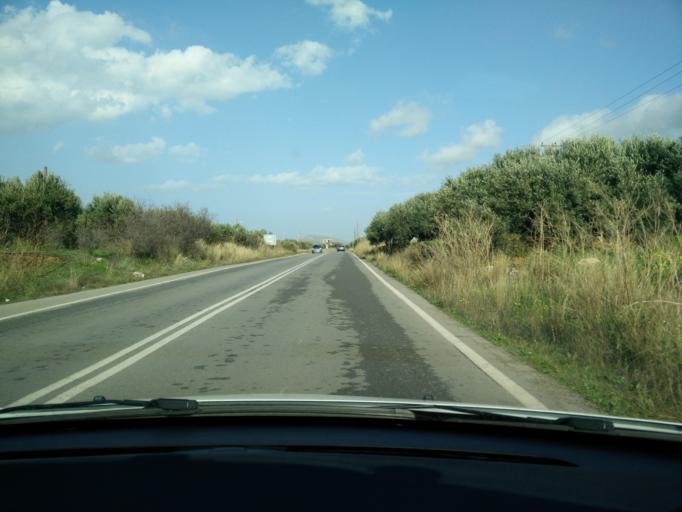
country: GR
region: Crete
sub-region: Nomos Lasithiou
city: Kato Chorio
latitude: 35.0643
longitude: 25.7988
